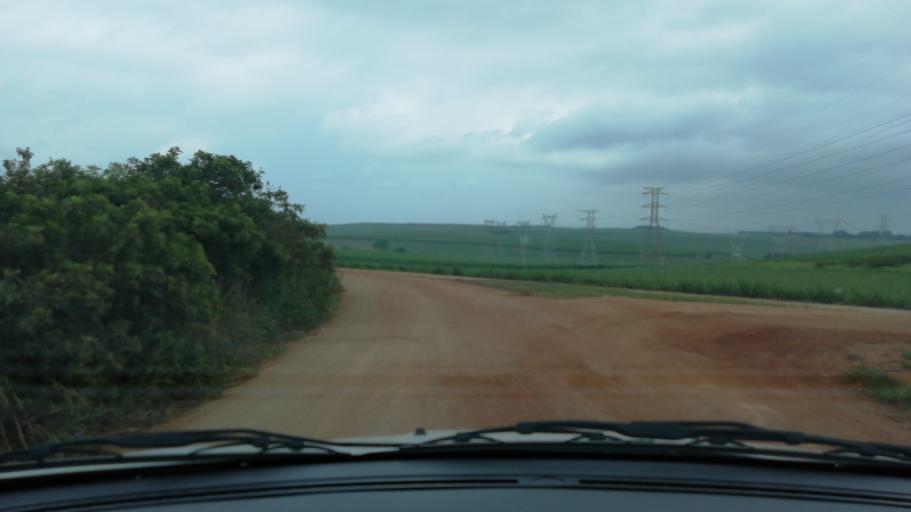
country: ZA
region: KwaZulu-Natal
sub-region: uThungulu District Municipality
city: Empangeni
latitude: -28.7296
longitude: 31.9082
